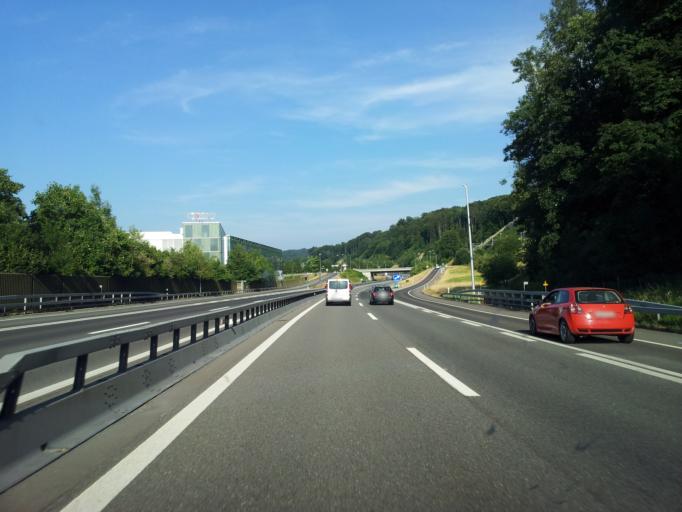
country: CH
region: Fribourg
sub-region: Sense District
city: Flamatt
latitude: 46.8893
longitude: 7.3185
